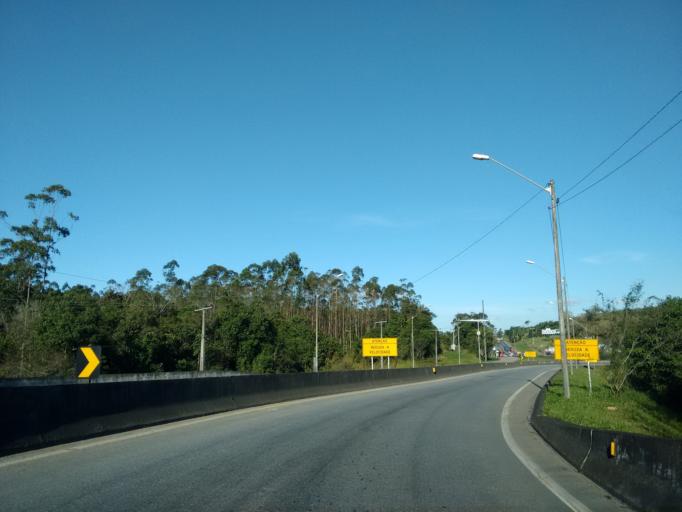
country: BR
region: Santa Catarina
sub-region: Joinville
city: Joinville
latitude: -26.4366
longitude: -48.8049
